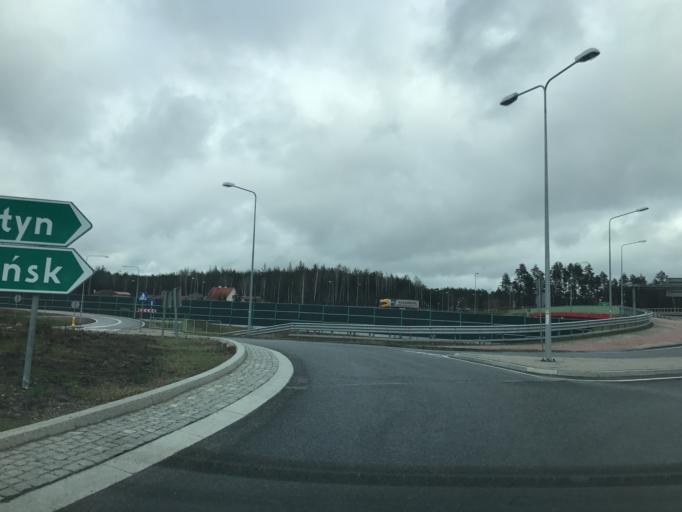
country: PL
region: Warmian-Masurian Voivodeship
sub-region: Powiat olsztynski
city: Olsztynek
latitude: 53.5326
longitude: 20.2744
